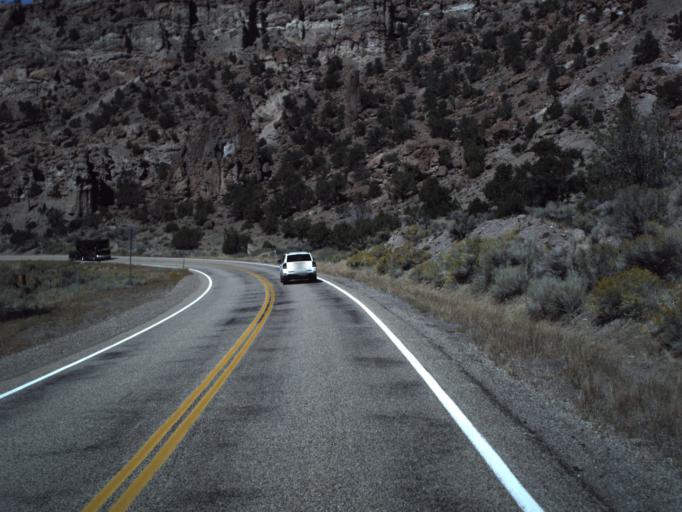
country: US
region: Utah
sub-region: Piute County
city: Junction
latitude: 38.1941
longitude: -112.1348
